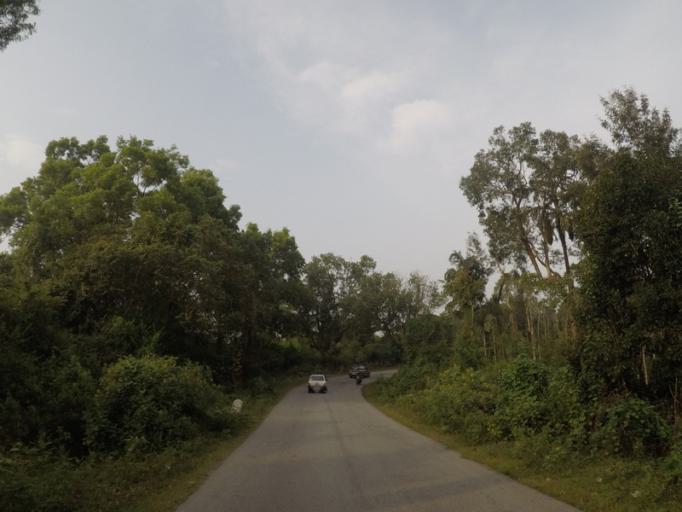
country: IN
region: Karnataka
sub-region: Chikmagalur
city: Chikmagalur
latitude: 13.2672
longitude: 75.6905
